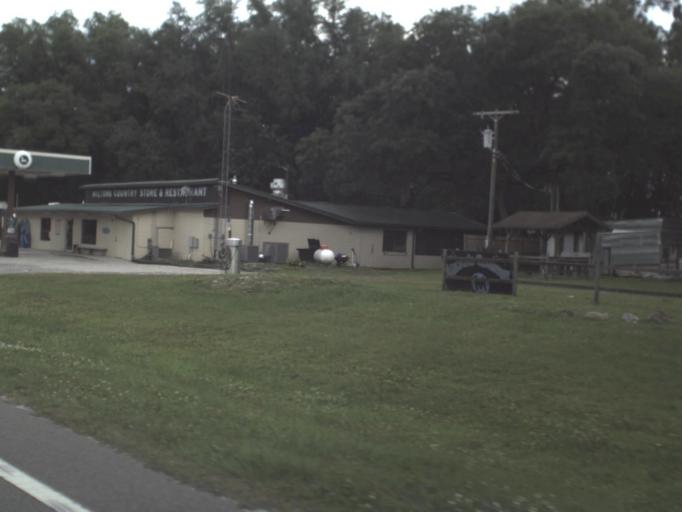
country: US
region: Florida
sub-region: Columbia County
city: Five Points
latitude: 30.3596
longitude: -82.6181
